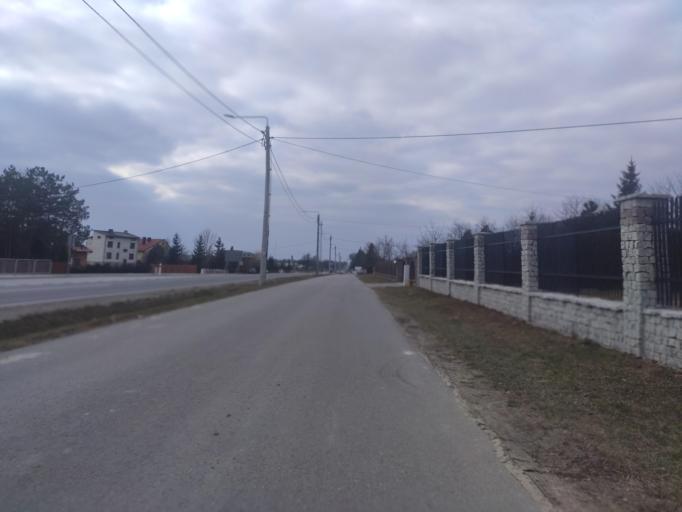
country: PL
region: Lublin Voivodeship
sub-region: Powiat lubartowski
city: Kock
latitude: 51.6437
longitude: 22.4347
